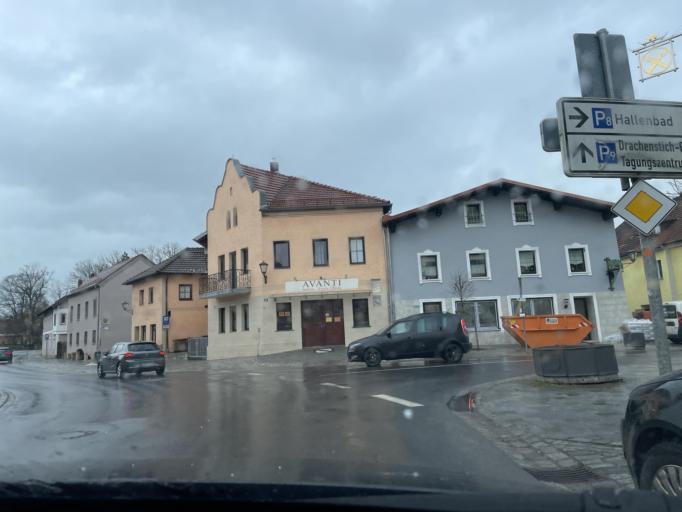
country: DE
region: Bavaria
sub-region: Upper Palatinate
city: Furth im Wald
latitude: 49.3064
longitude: 12.8455
